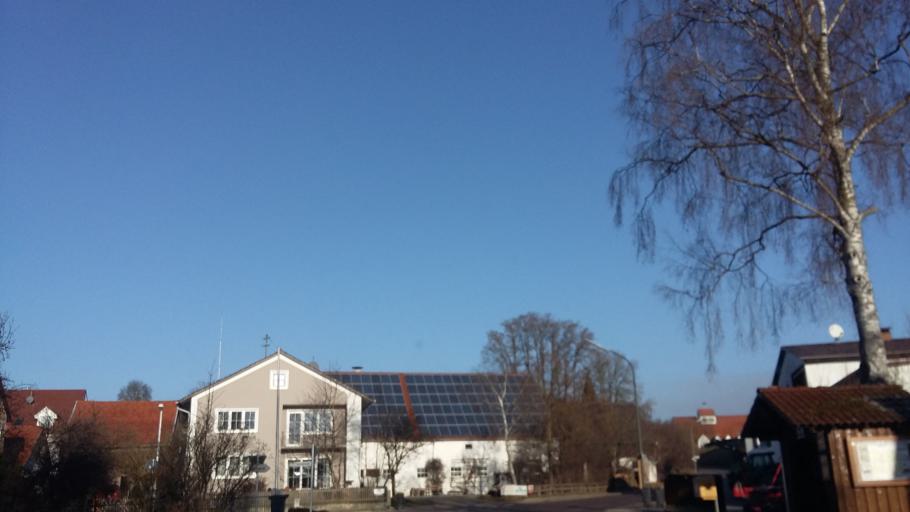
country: DE
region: Bavaria
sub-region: Swabia
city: Adelzhausen
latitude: 48.3567
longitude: 11.1377
